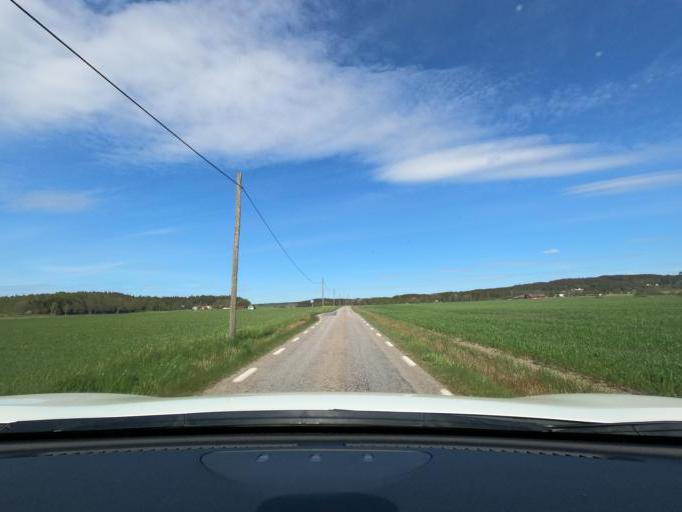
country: SE
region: Vaestra Goetaland
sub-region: Marks Kommun
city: Horred
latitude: 57.4547
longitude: 12.4902
